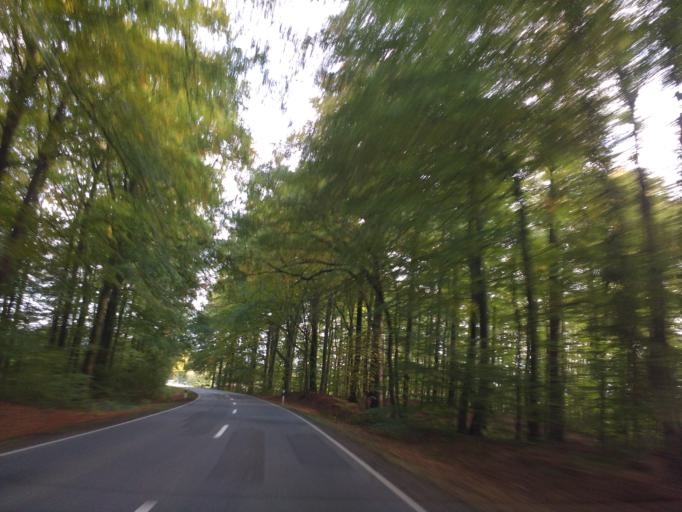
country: DE
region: Schleswig-Holstein
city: Schonwalde am Bungsberg
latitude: 54.2042
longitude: 10.7467
